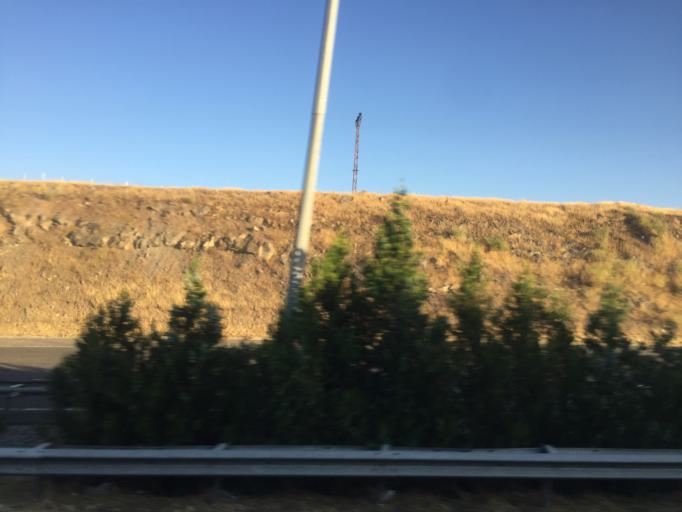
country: TR
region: Sanliurfa
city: Bogurtlen
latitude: 37.1008
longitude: 38.2001
